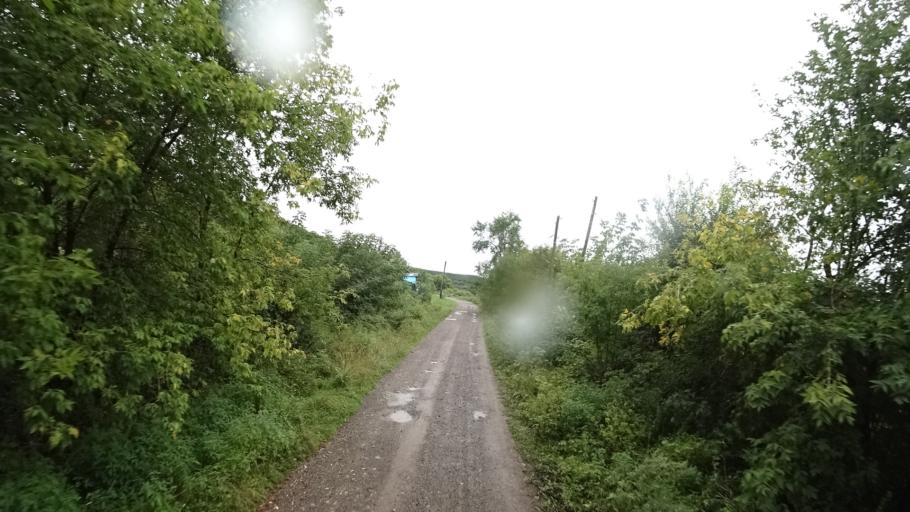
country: RU
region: Primorskiy
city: Monastyrishche
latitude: 44.2625
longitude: 132.4051
